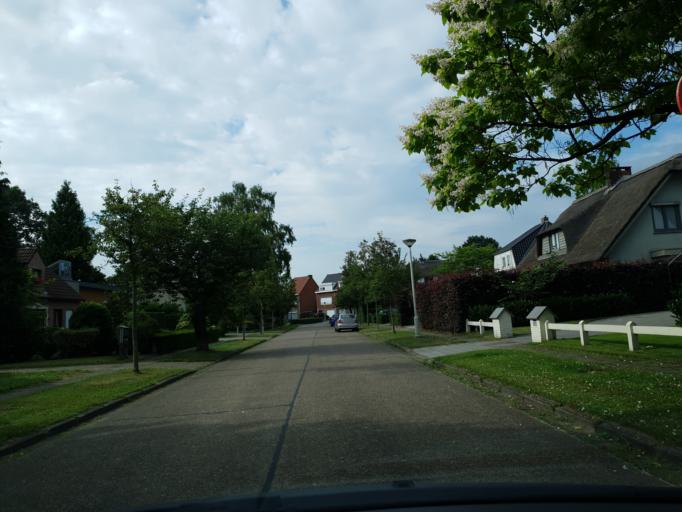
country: BE
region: Flanders
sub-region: Provincie Antwerpen
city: Kapellen
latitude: 51.2734
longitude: 4.4501
